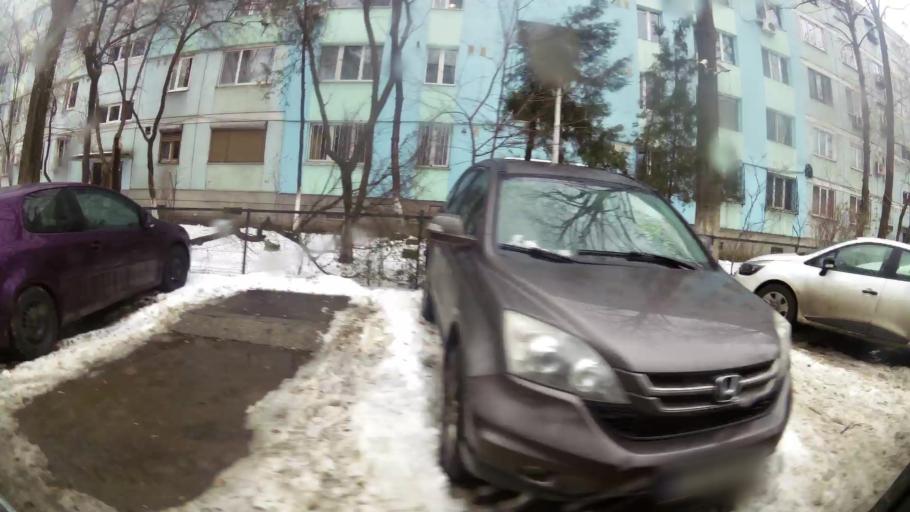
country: RO
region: Ilfov
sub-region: Comuna Chiajna
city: Rosu
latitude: 44.4172
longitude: 26.0173
